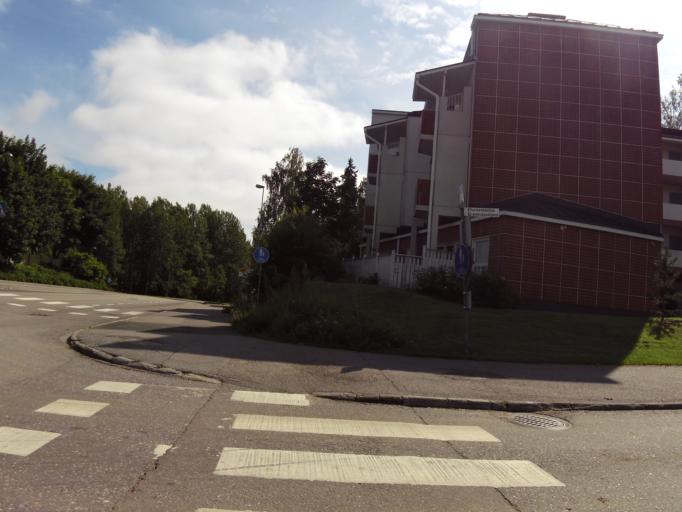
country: FI
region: Uusimaa
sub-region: Helsinki
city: Koukkuniemi
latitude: 60.1605
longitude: 24.7249
